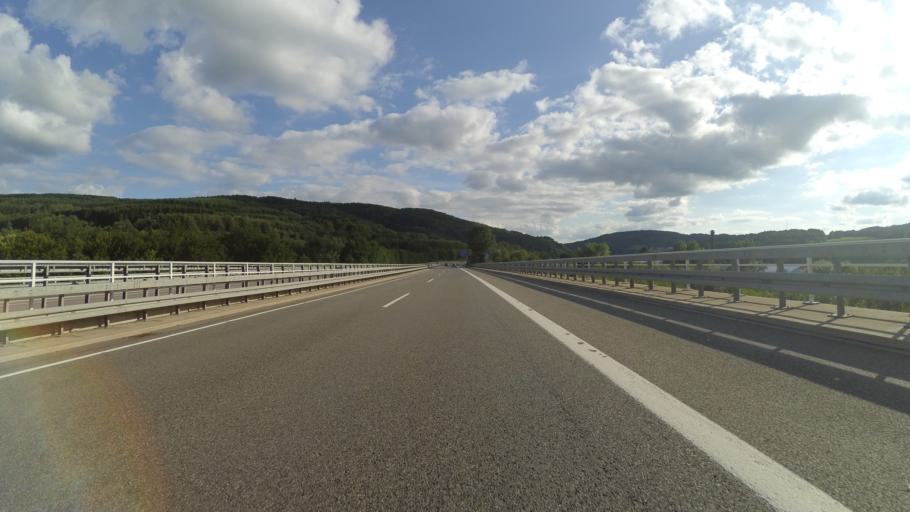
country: DE
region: Saarland
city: Nonnweiler
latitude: 49.5817
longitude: 6.9837
